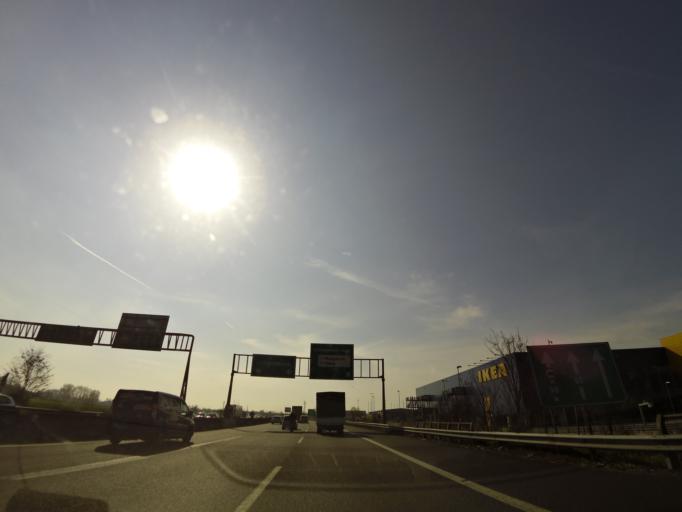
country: IT
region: Lombardy
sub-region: Citta metropolitana di Milano
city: Chiaravalle
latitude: 45.4474
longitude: 9.2388
